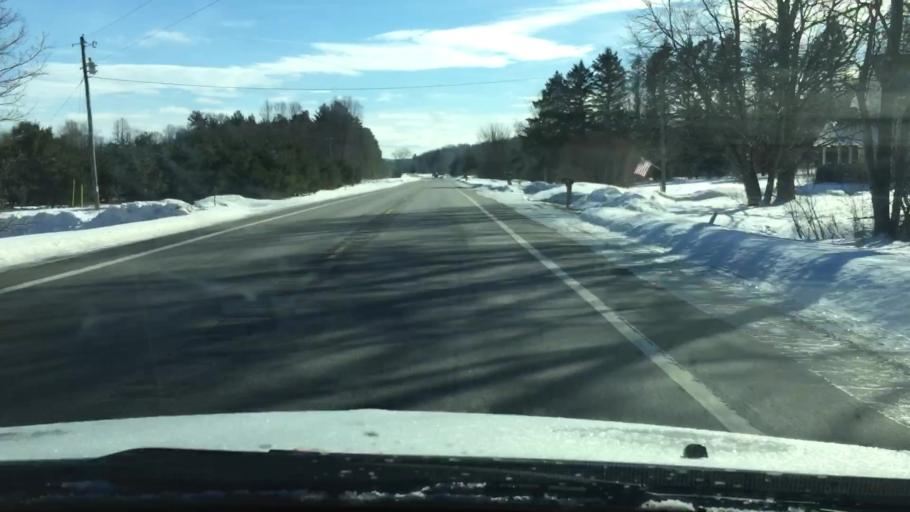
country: US
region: Michigan
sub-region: Charlevoix County
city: East Jordan
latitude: 45.0783
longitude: -85.0884
